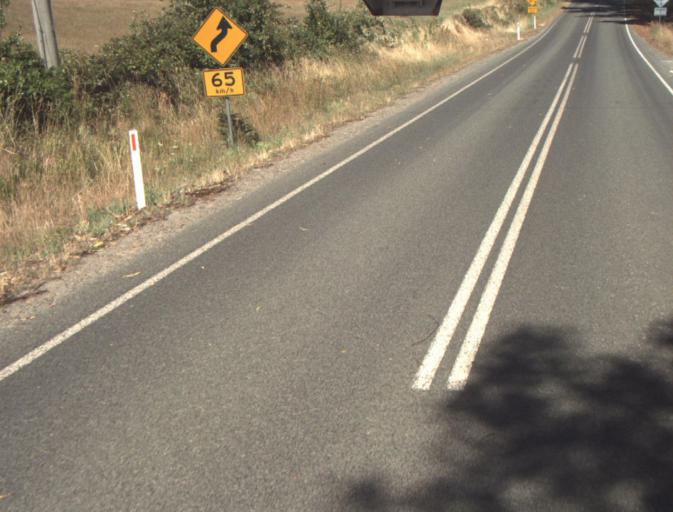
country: AU
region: Tasmania
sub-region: Launceston
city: Newstead
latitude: -41.3260
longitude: 147.3569
